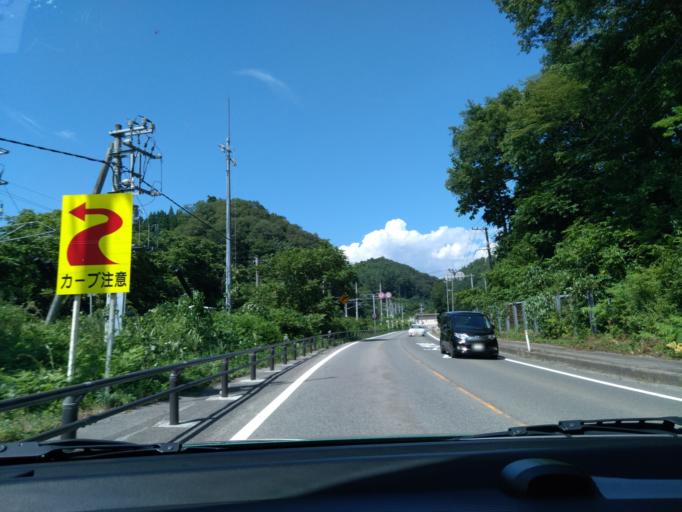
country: JP
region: Akita
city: Kakunodatemachi
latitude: 39.6802
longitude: 140.7034
